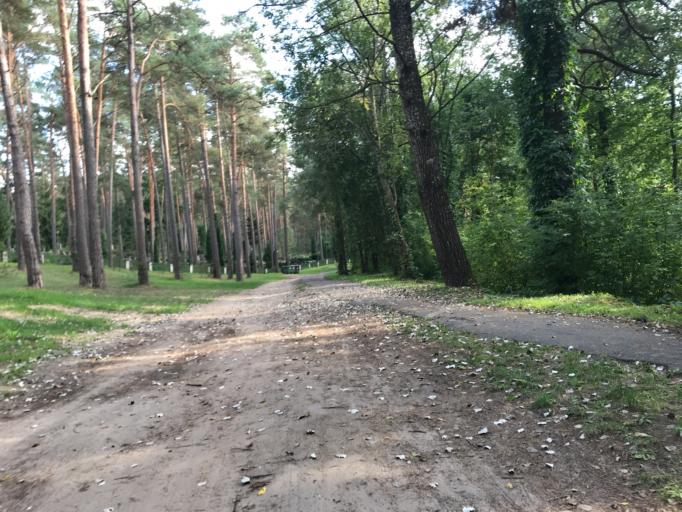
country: LT
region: Alytaus apskritis
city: Druskininkai
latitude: 54.0133
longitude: 23.9705
